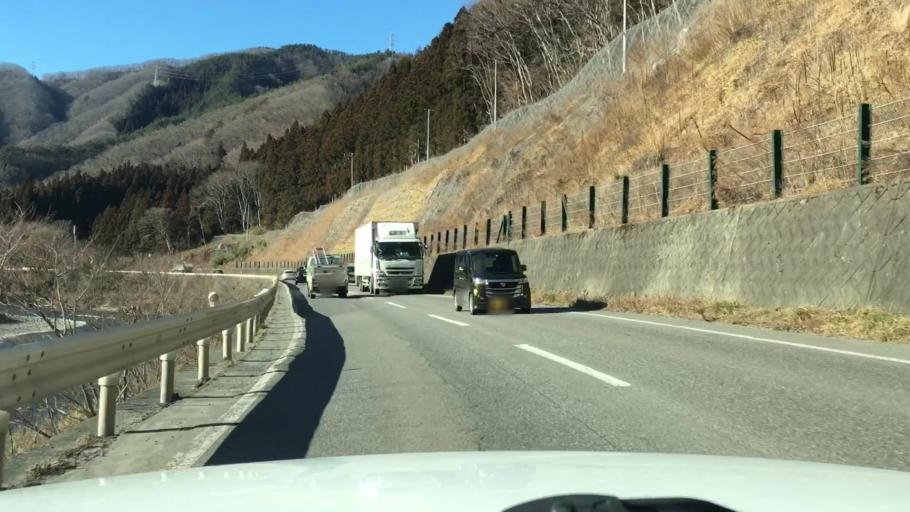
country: JP
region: Iwate
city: Miyako
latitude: 39.6269
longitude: 141.8233
